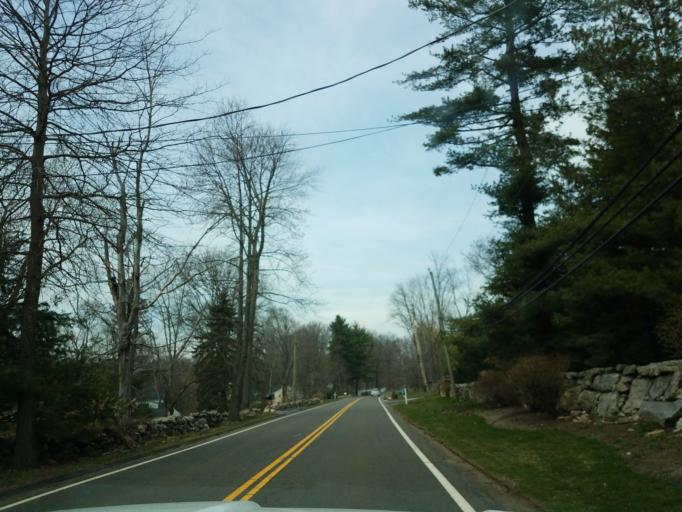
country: US
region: Connecticut
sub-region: Fairfield County
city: Glenville
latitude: 41.0919
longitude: -73.6479
